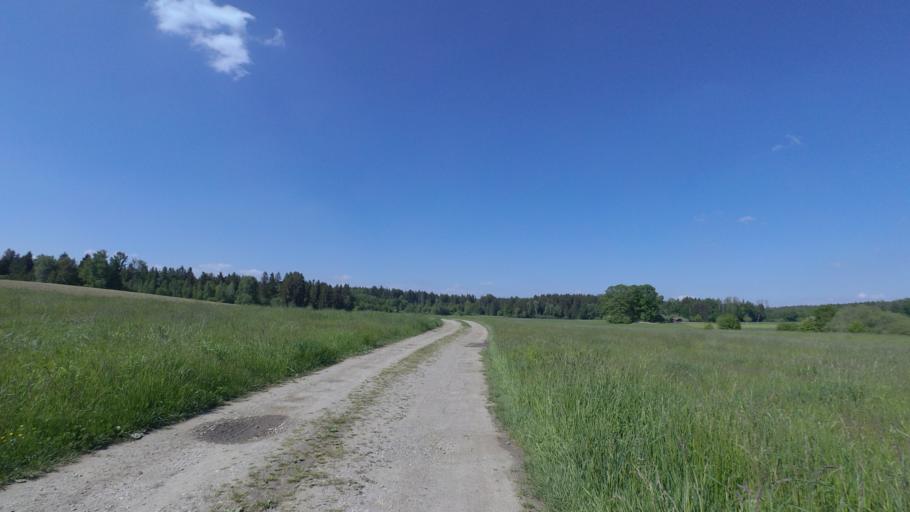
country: DE
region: Bavaria
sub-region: Upper Bavaria
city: Chieming
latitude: 47.9106
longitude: 12.5086
